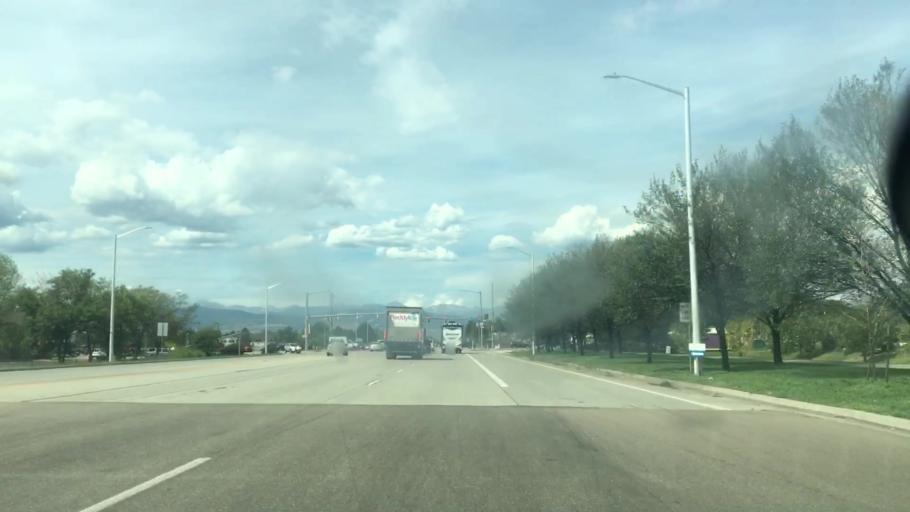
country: US
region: Colorado
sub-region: Boulder County
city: Longmont
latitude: 40.2034
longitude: -105.1005
